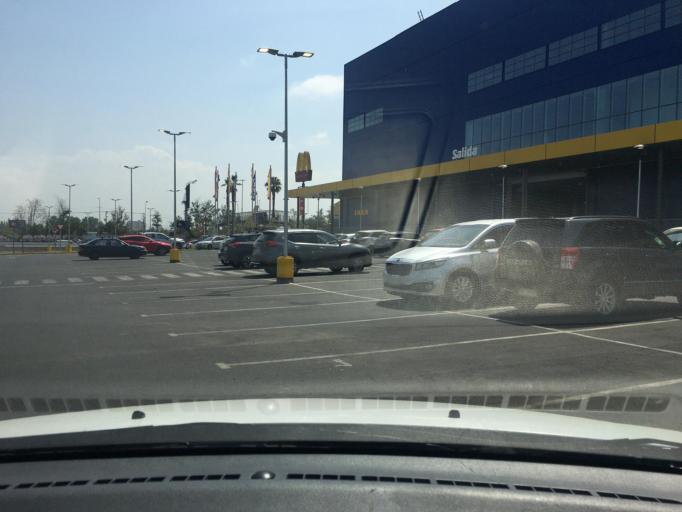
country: CL
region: Santiago Metropolitan
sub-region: Provincia de Santiago
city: Lo Prado
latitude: -33.5172
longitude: -70.7150
